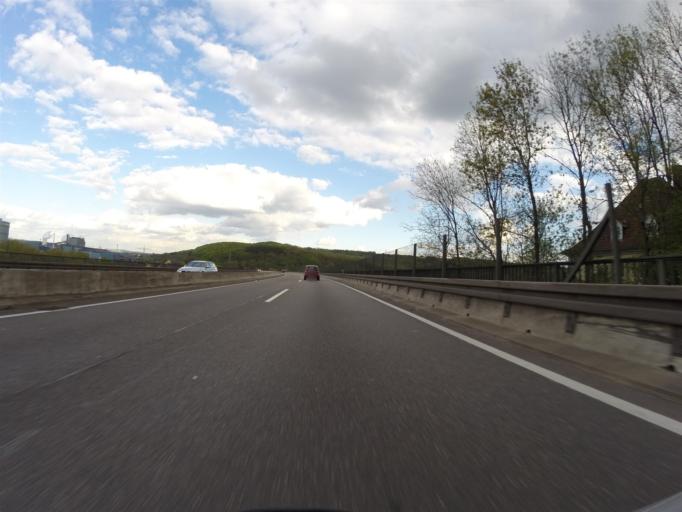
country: DE
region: Saarland
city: Volklingen
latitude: 49.2428
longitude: 6.8375
